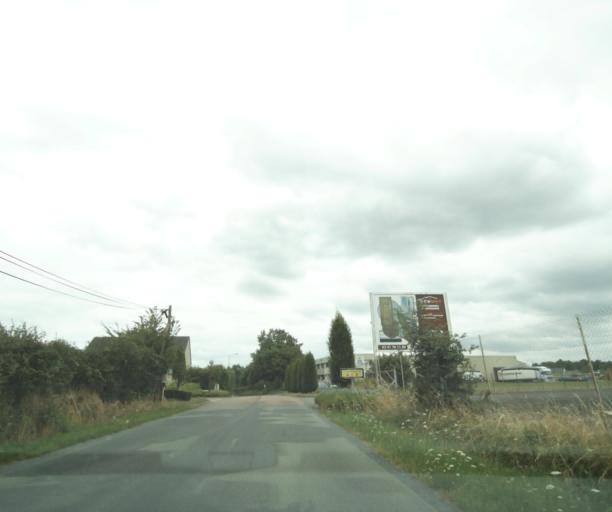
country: FR
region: Pays de la Loire
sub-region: Departement de Maine-et-Loire
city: Durtal
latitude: 47.6746
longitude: -0.2492
